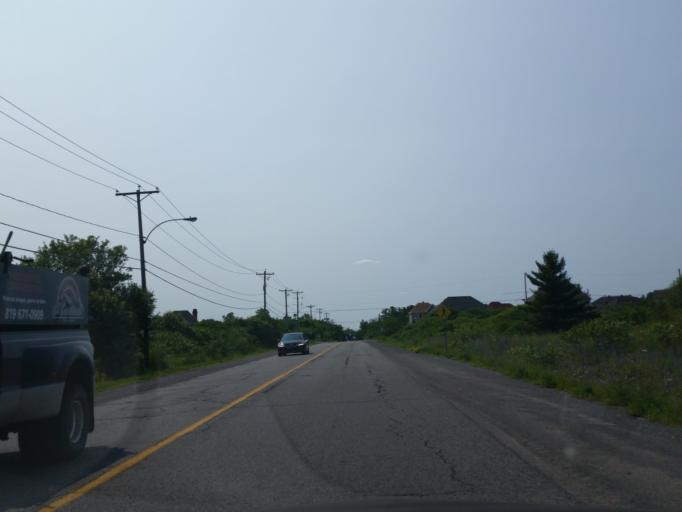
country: CA
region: Ontario
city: Bells Corners
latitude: 45.3858
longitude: -75.8279
